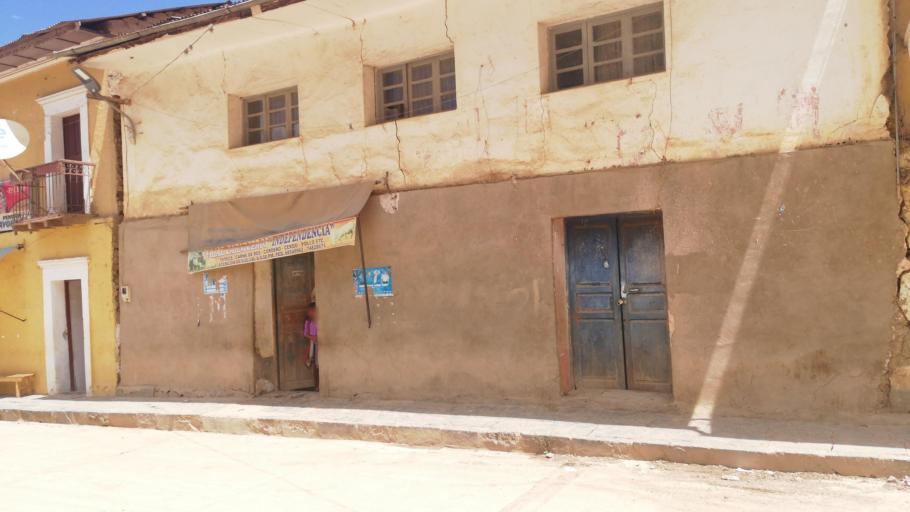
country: BO
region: Cochabamba
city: Colchani
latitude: -17.0844
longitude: -66.8195
